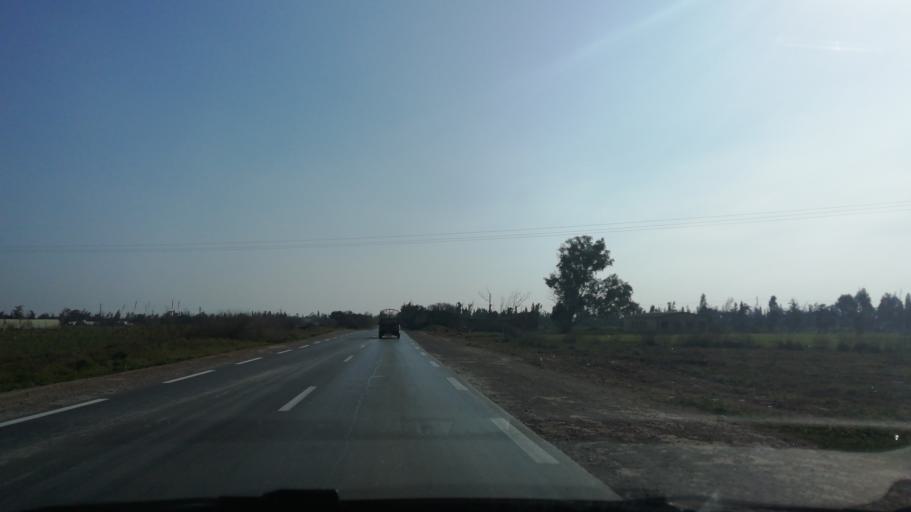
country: DZ
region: Mostaganem
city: Mostaganem
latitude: 35.7432
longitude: -0.0190
